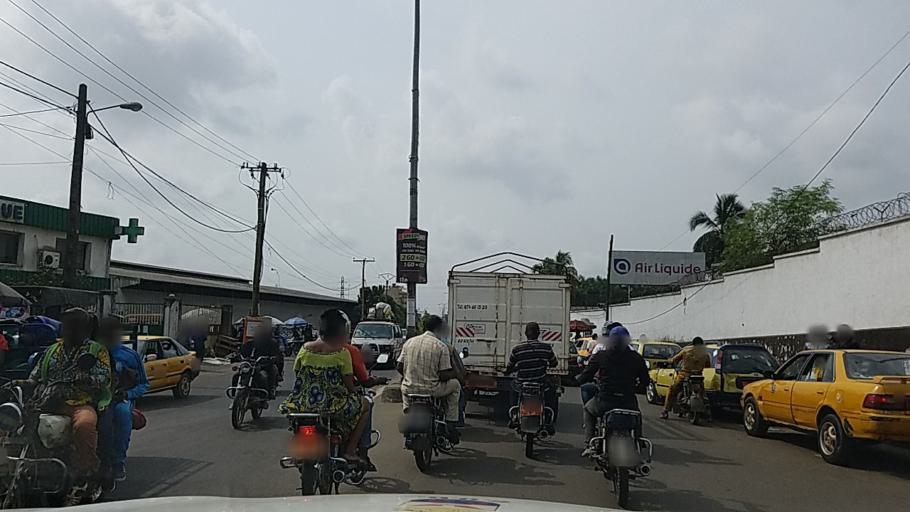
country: CM
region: Littoral
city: Douala
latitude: 4.0417
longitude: 9.7424
